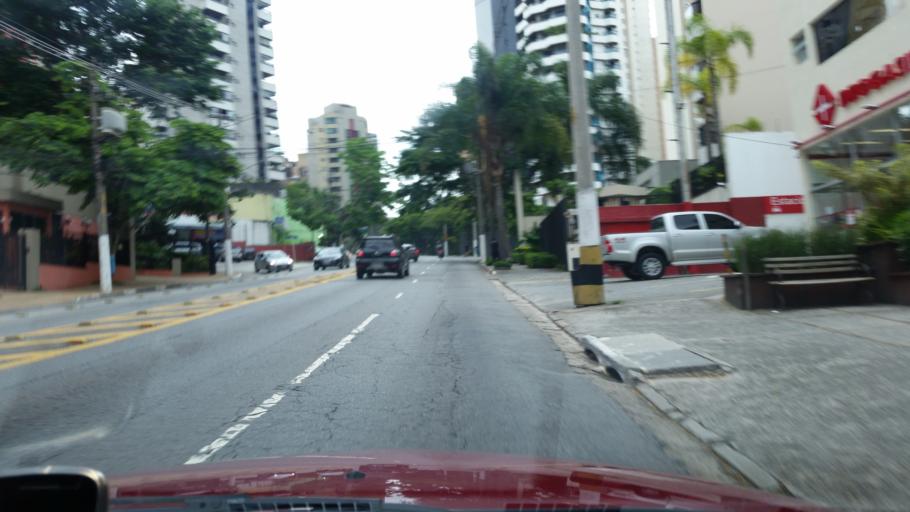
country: BR
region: Sao Paulo
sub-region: Taboao Da Serra
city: Taboao da Serra
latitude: -23.6334
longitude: -46.7305
